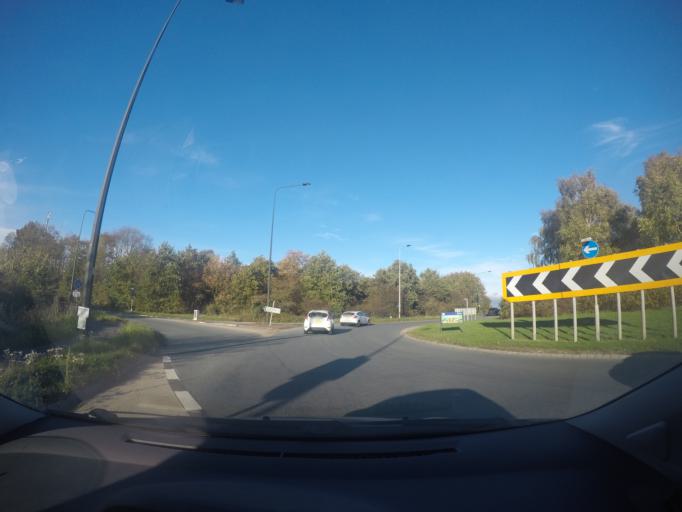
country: GB
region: England
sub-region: City of York
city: Copmanthorpe
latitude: 53.9207
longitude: -1.1527
